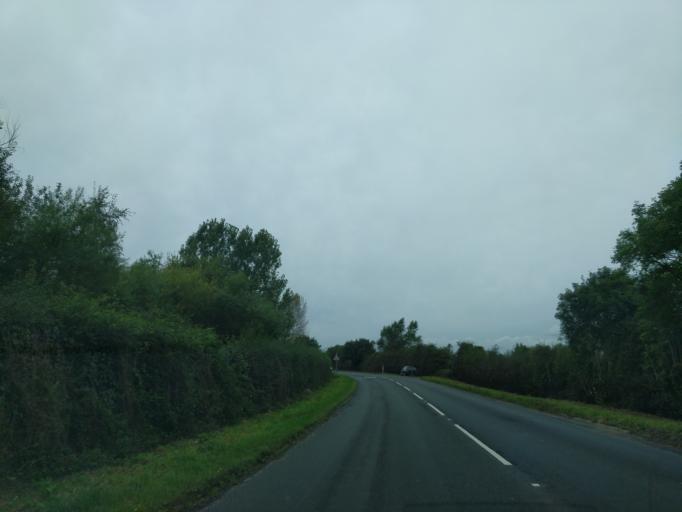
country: GB
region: England
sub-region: Cheshire East
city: Weston
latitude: 53.0557
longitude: -2.3867
